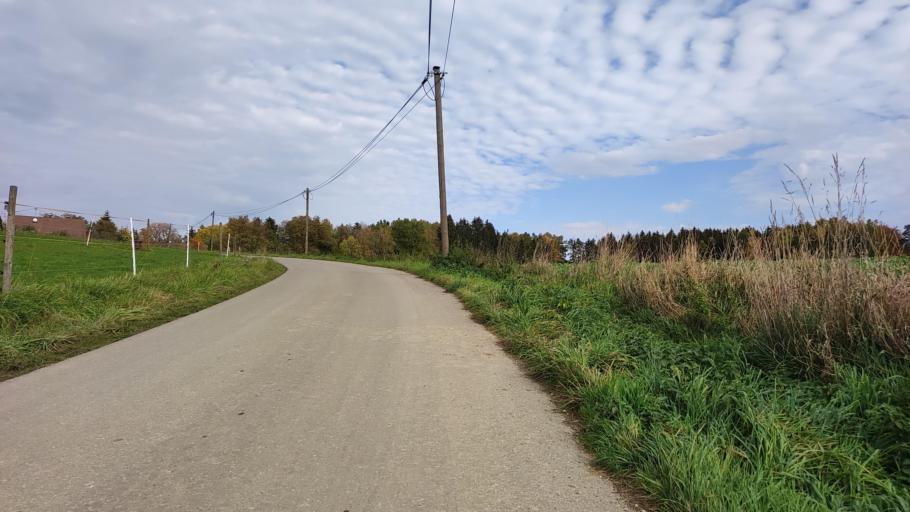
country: DE
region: Bavaria
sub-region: Swabia
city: Munsterhausen
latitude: 48.3203
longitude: 10.4804
